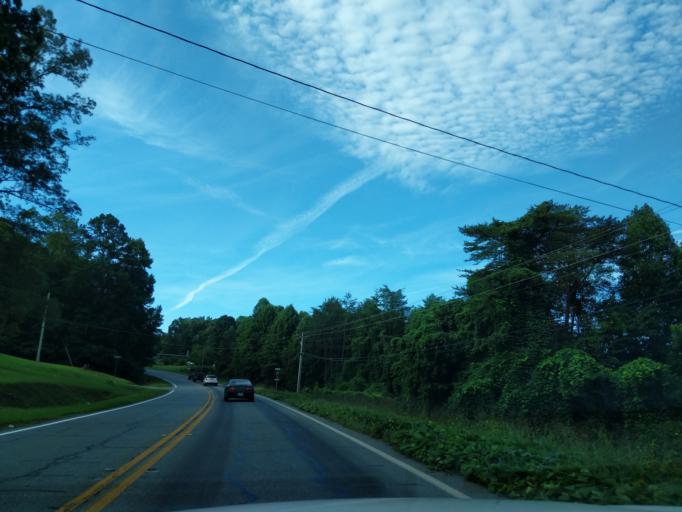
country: US
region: Georgia
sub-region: Fannin County
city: Blue Ridge
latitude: 34.9103
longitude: -84.3770
